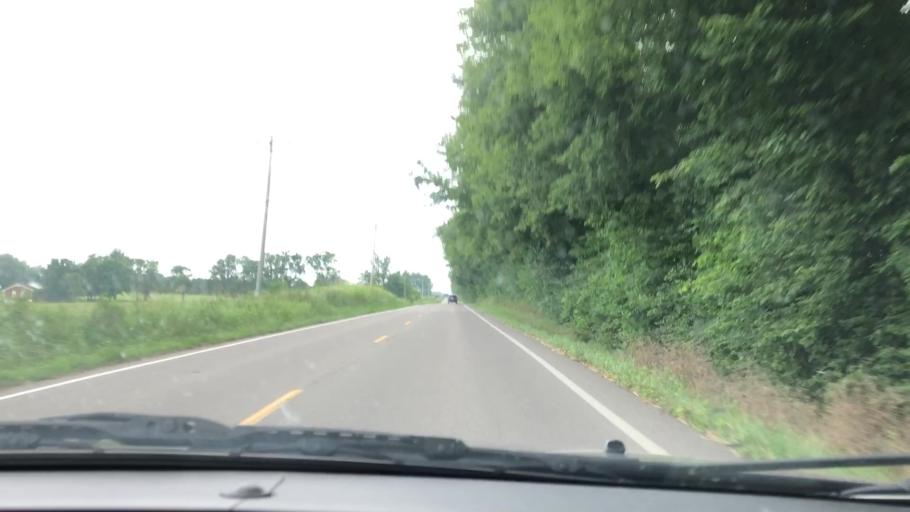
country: US
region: Tennessee
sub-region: Maury County
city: Spring Hill
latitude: 35.7417
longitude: -87.0097
